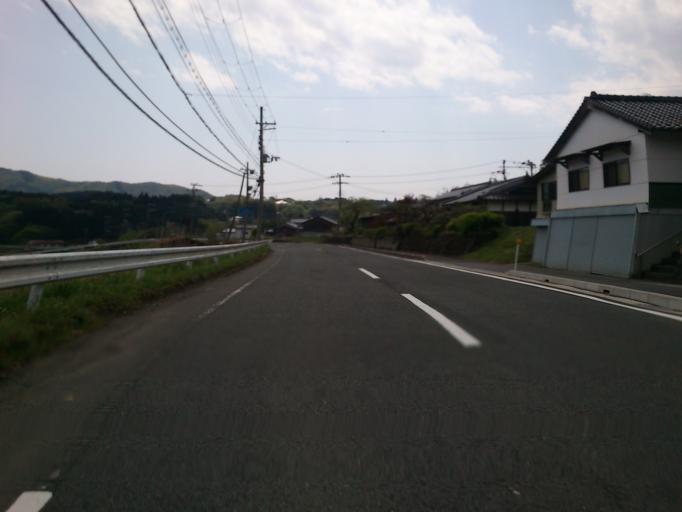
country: JP
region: Kyoto
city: Fukuchiyama
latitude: 35.3449
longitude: 134.9398
